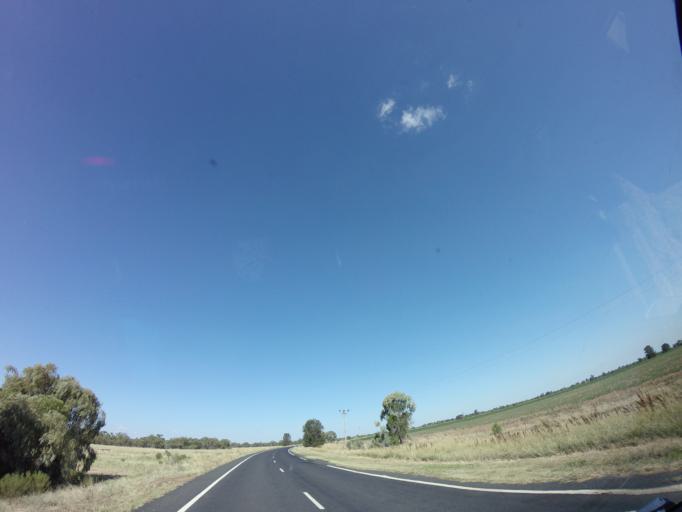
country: AU
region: New South Wales
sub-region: Gilgandra
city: Gilgandra
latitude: -31.6644
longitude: 148.1751
